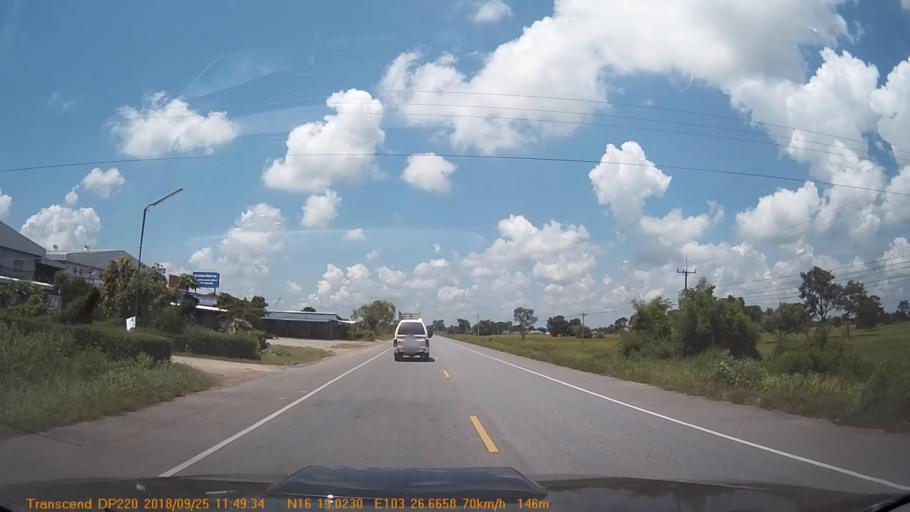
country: TH
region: Kalasin
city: Khong Chai
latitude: 16.3171
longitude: 103.4445
